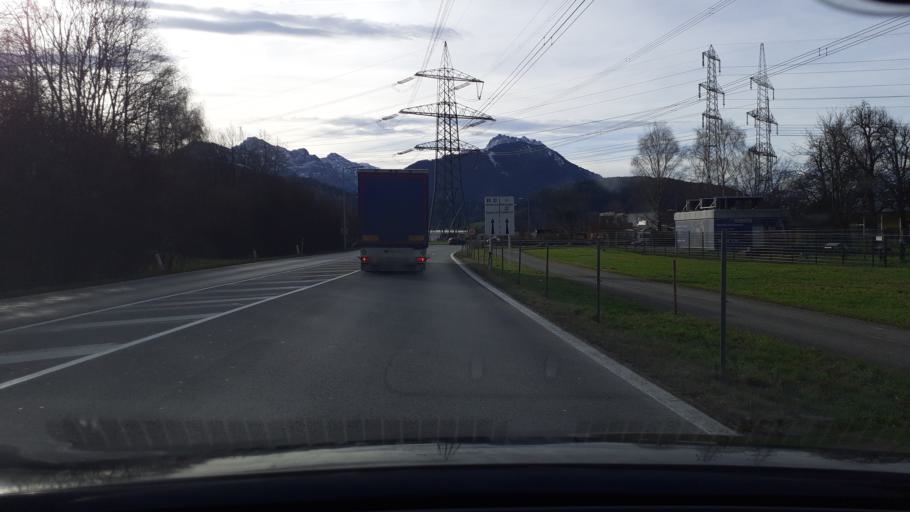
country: AT
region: Vorarlberg
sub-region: Politischer Bezirk Feldkirch
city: Rankweil
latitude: 47.2741
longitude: 9.6211
